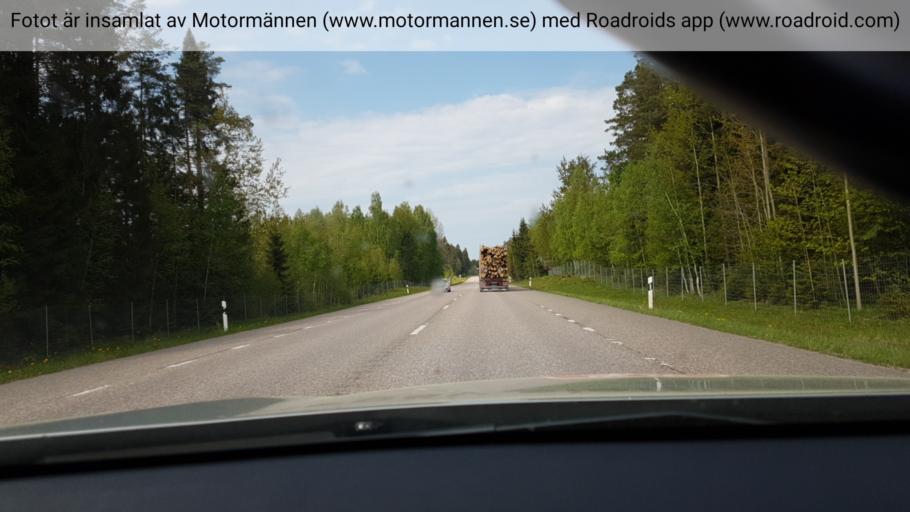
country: SE
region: Uppsala
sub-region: Alvkarleby Kommun
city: AElvkarleby
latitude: 60.5895
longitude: 17.4640
